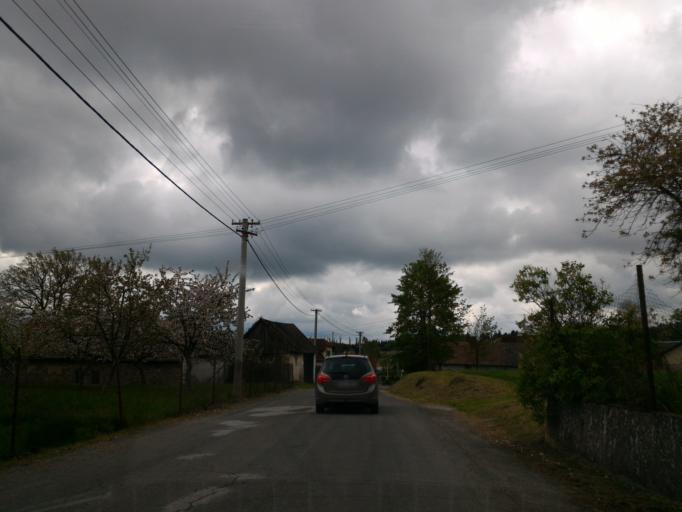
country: CZ
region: Vysocina
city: Ledec nad Sazavou
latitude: 49.6300
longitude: 15.2928
